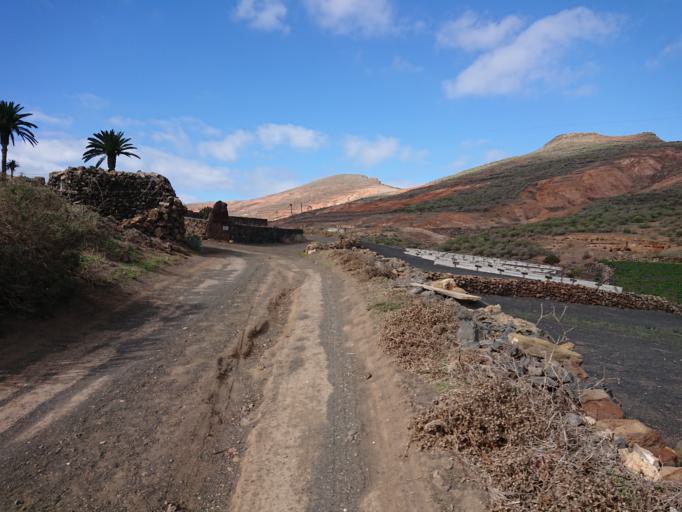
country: ES
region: Canary Islands
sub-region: Provincia de Las Palmas
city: Haria
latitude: 29.1439
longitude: -13.5087
